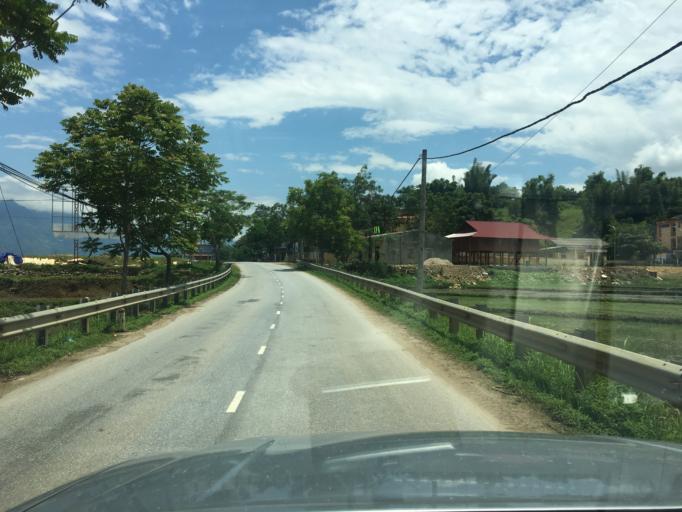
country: VN
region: Yen Bai
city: Son Thinh
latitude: 21.6203
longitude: 104.5088
